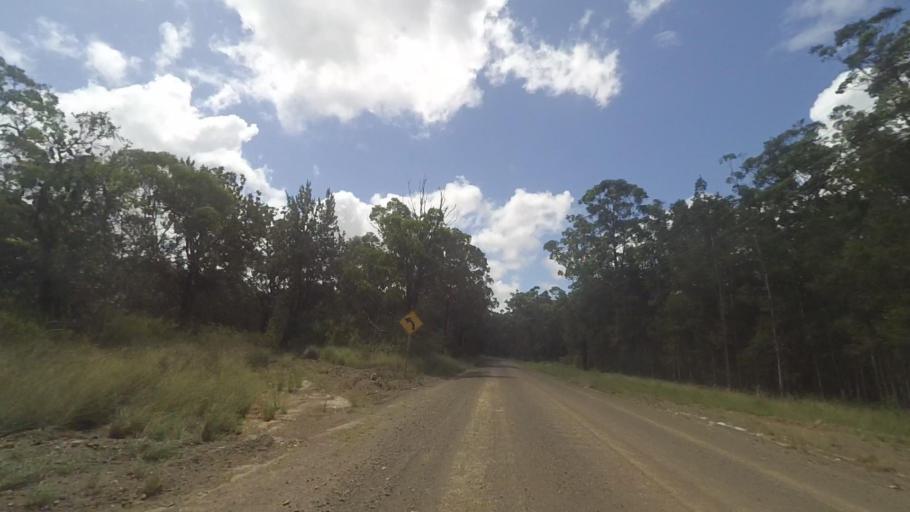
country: AU
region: New South Wales
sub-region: Great Lakes
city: Bulahdelah
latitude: -32.5041
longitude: 152.2907
